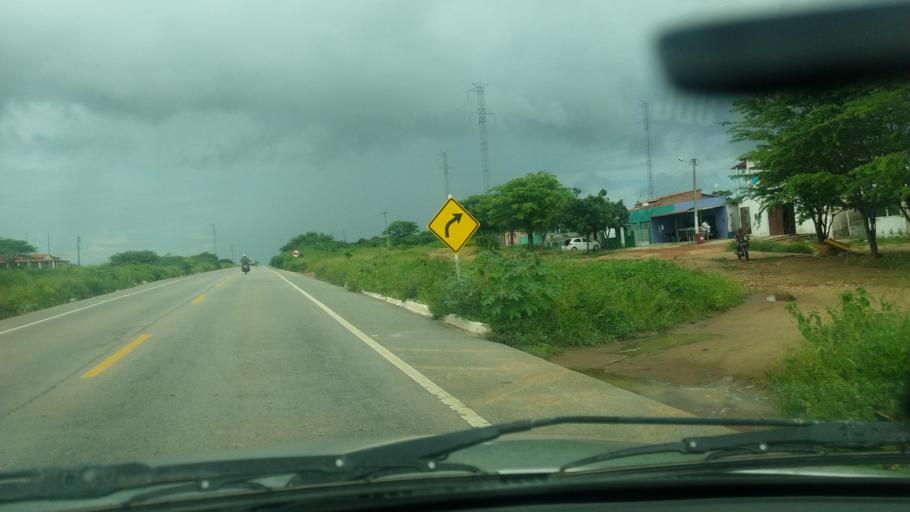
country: BR
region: Rio Grande do Norte
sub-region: Santa Cruz
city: Santa Cruz
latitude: -6.1935
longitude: -36.2104
